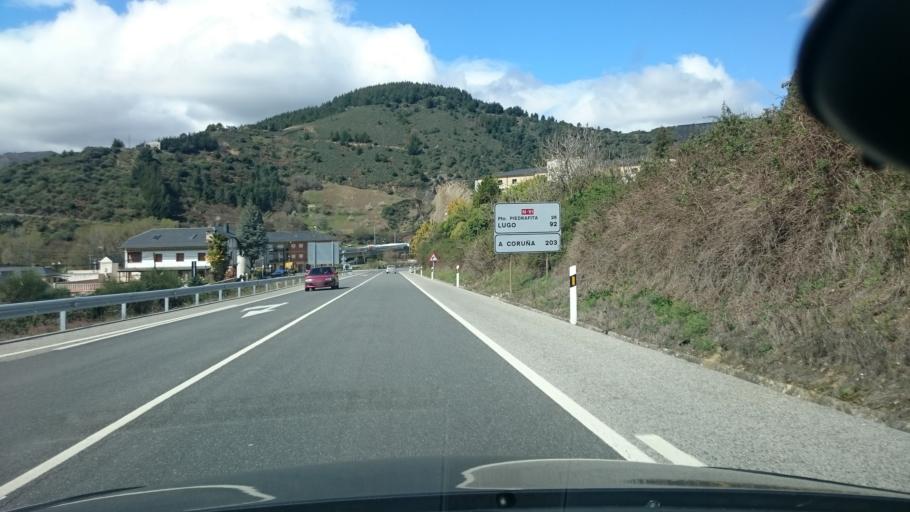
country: ES
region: Castille and Leon
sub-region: Provincia de Leon
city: Villafranca del Bierzo
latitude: 42.6024
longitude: -6.8125
